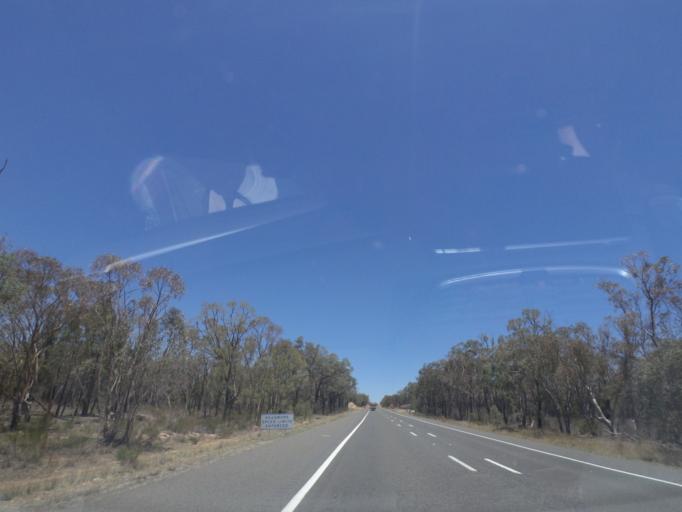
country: AU
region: New South Wales
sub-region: Warrumbungle Shire
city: Coonabarabran
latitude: -30.9162
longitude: 149.4342
